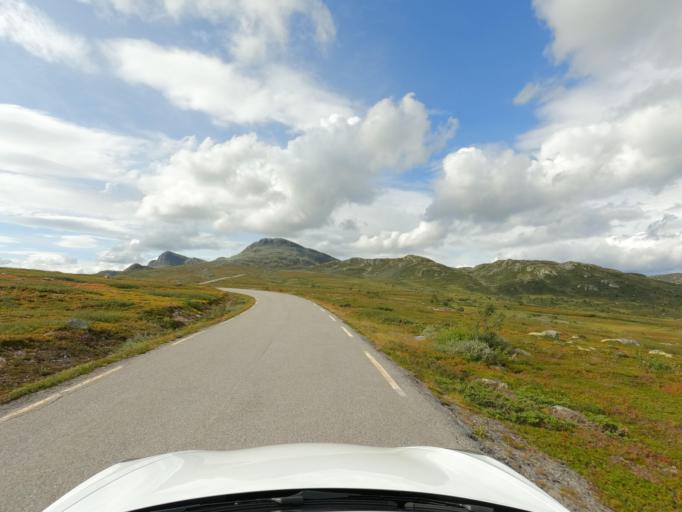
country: NO
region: Telemark
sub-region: Tinn
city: Rjukan
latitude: 59.8077
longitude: 8.7542
